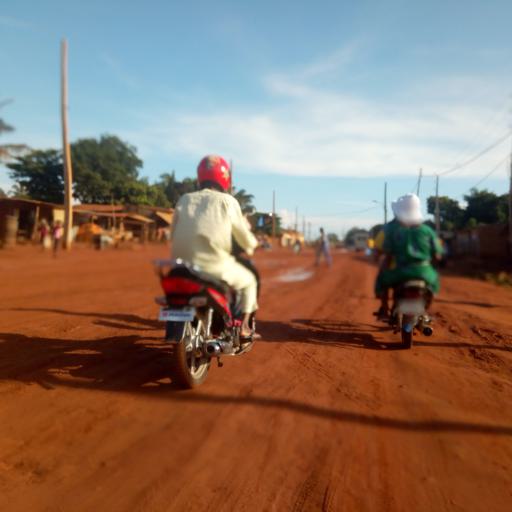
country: BJ
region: Atlantique
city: Hevie
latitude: 6.4167
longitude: 2.2630
